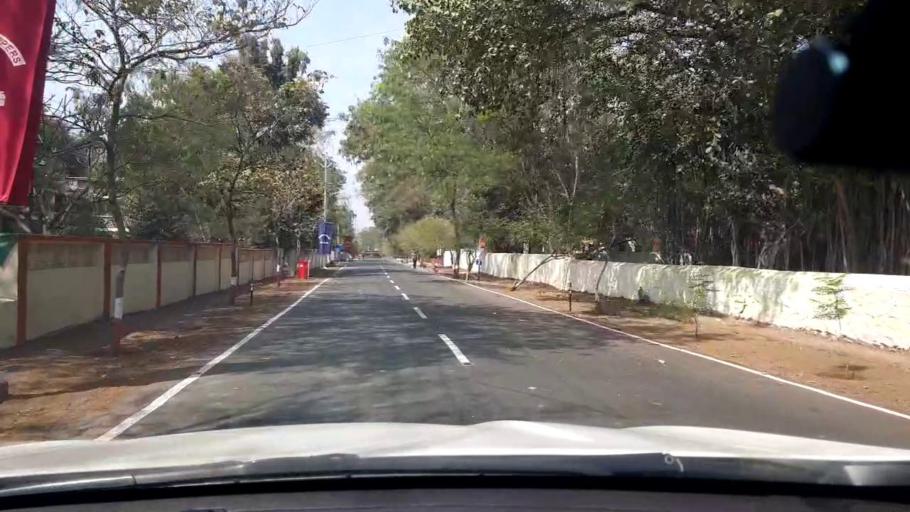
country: IN
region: Maharashtra
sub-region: Pune Division
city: Shivaji Nagar
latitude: 18.5462
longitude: 73.8631
